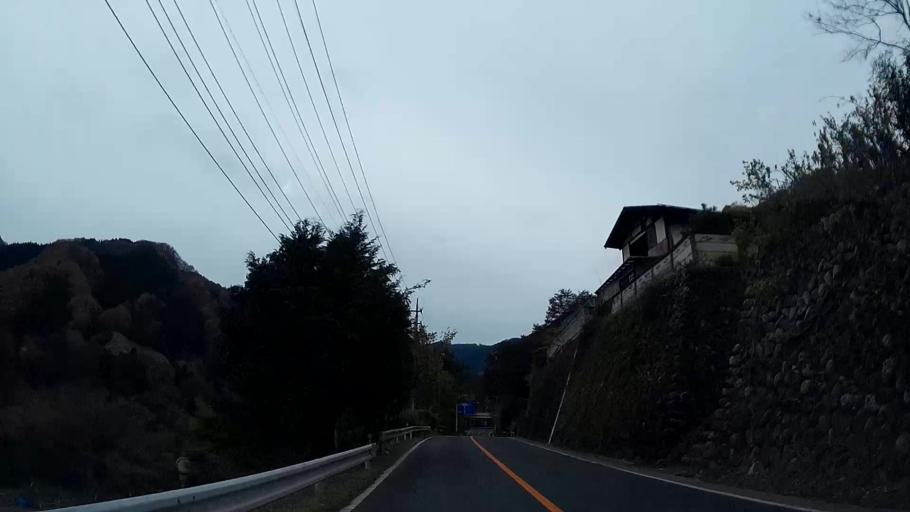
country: JP
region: Saitama
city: Chichibu
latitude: 35.9632
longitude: 138.9773
